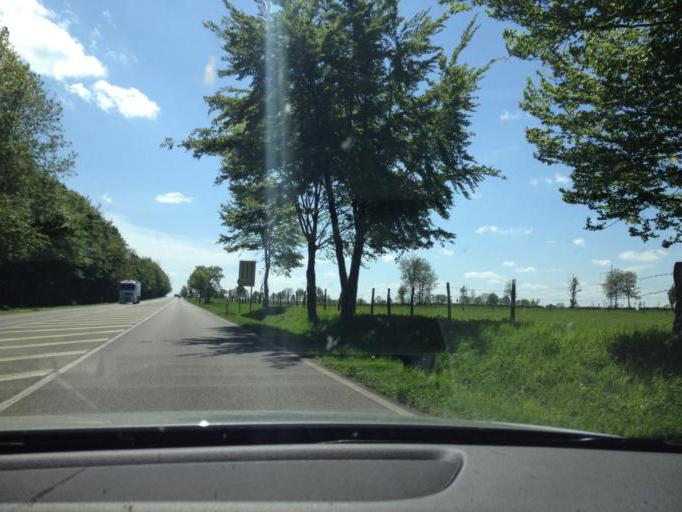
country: DE
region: North Rhine-Westphalia
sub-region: Regierungsbezirk Koln
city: Dahlem
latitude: 50.4128
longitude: 6.5771
